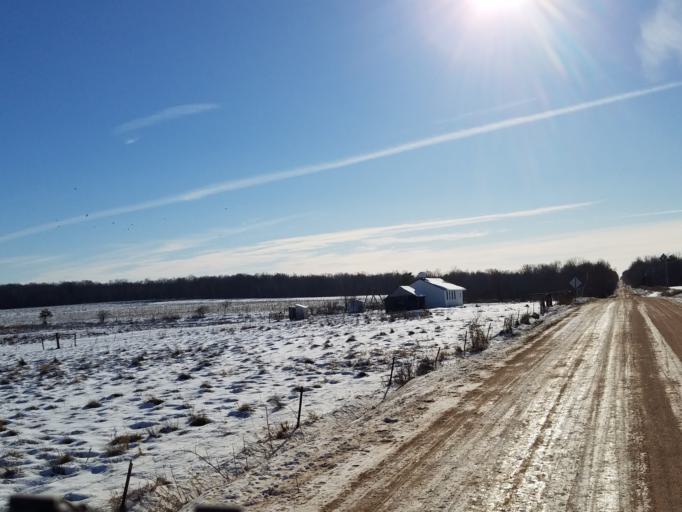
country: US
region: Wisconsin
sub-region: Clark County
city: Neillsville
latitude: 44.5665
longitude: -90.4164
